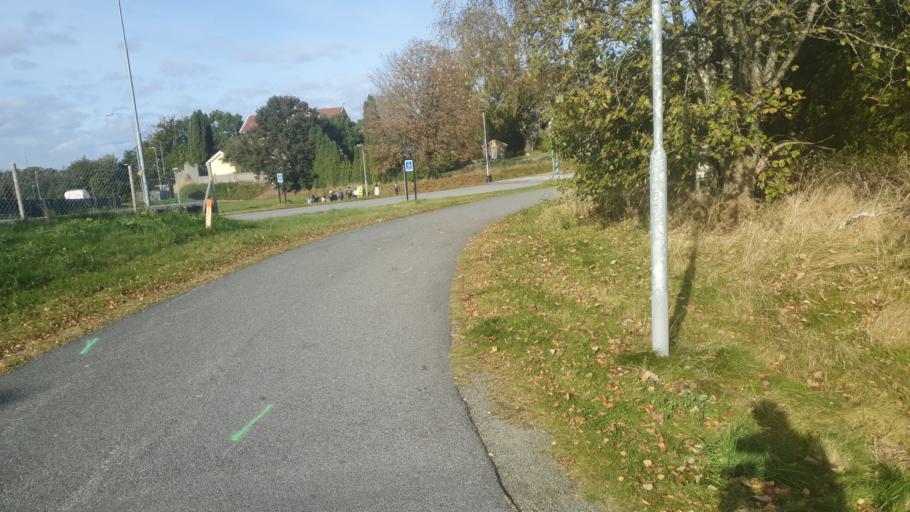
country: SE
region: Vaestra Goetaland
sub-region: Harryda Kommun
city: Molnlycke
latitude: 57.6555
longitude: 12.1280
